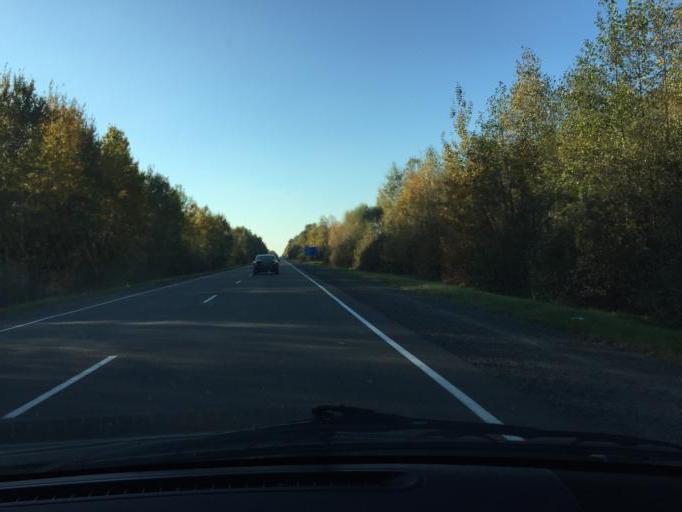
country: BY
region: Brest
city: Horad Luninyets
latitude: 52.2998
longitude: 26.7268
